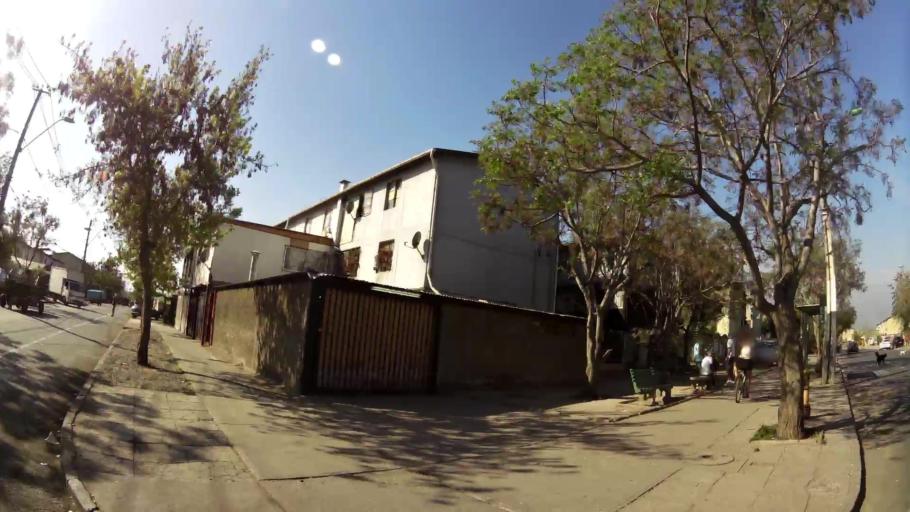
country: CL
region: Santiago Metropolitan
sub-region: Provincia de Santiago
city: La Pintana
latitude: -33.5619
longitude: -70.6182
